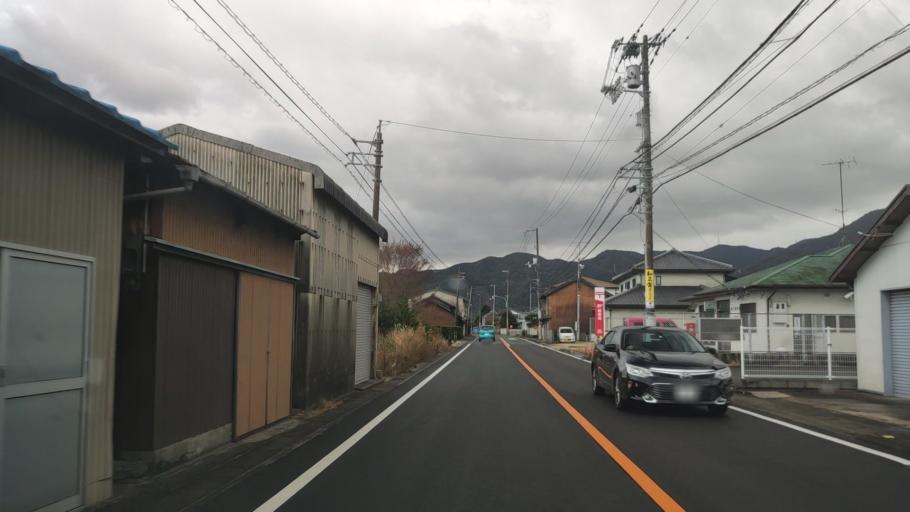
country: JP
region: Tokushima
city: Ishii
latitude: 34.2175
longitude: 134.4175
